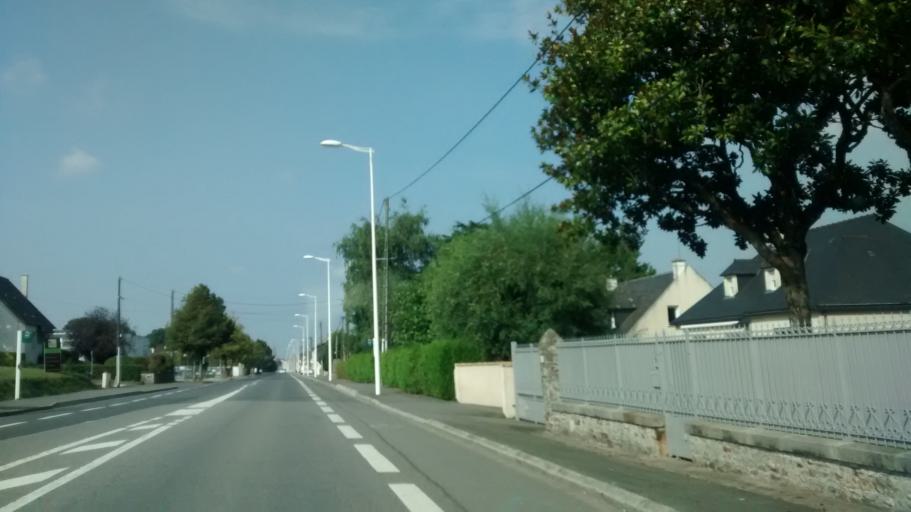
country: FR
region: Brittany
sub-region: Departement d'Ille-et-Vilaine
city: Vitre
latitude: 48.1221
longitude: -1.1873
